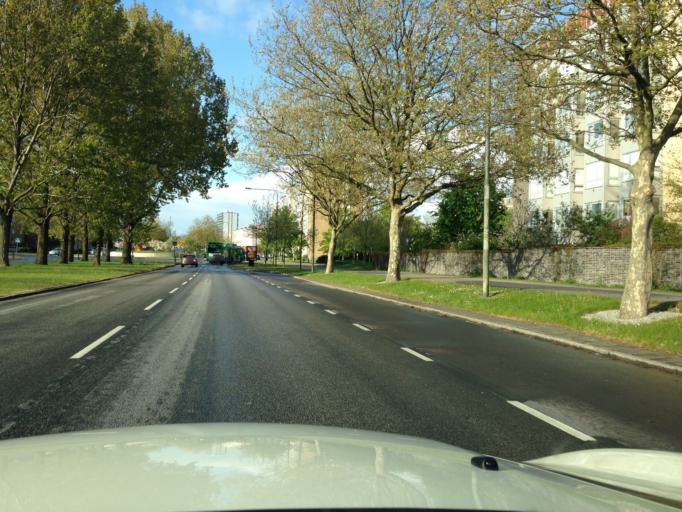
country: SE
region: Skane
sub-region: Malmo
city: Malmoe
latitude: 55.5822
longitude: 12.9788
